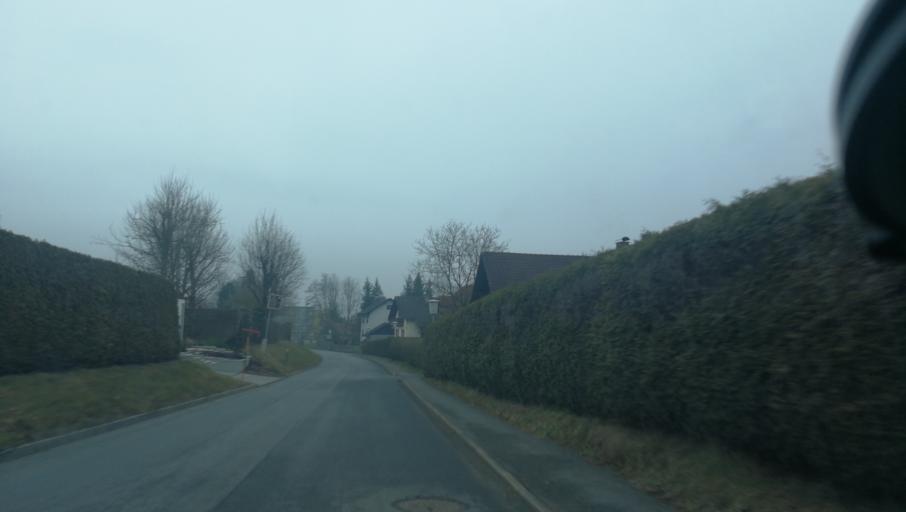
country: AT
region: Styria
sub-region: Politischer Bezirk Deutschlandsberg
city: Stainz
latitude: 46.8935
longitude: 15.2536
